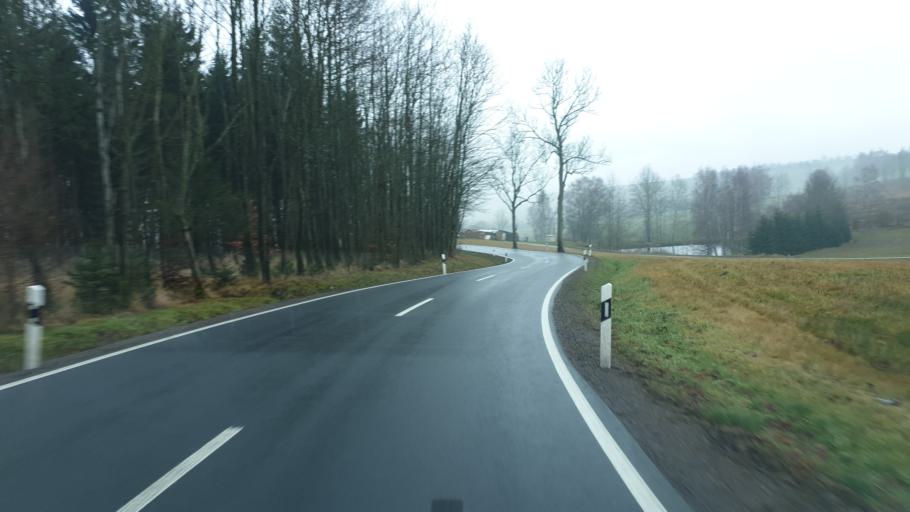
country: DE
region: Saxony
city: Neuhausen
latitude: 50.6911
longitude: 13.4605
